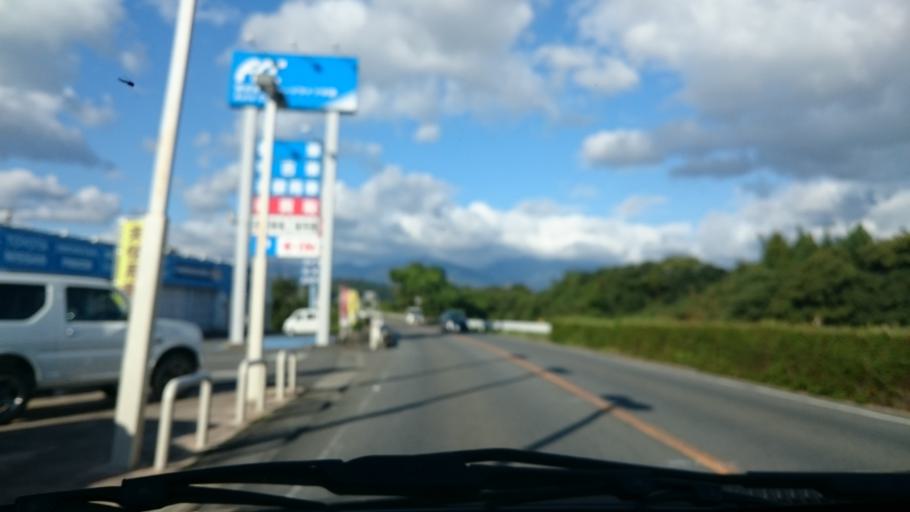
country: JP
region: Mie
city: Komono
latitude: 34.9795
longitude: 136.5647
